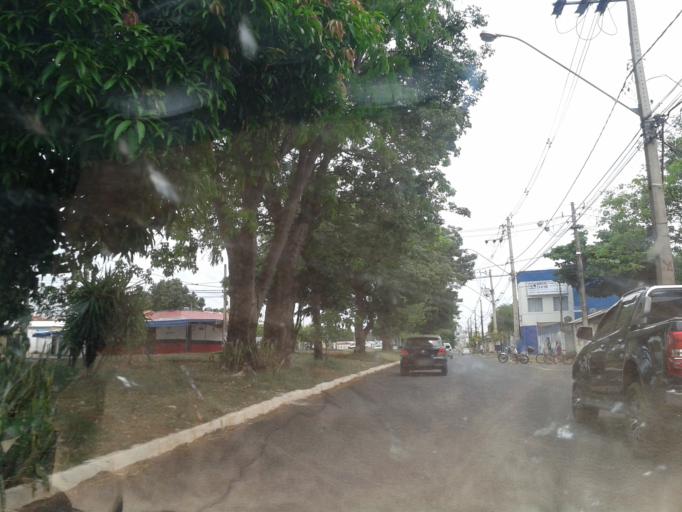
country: BR
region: Minas Gerais
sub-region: Uberlandia
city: Uberlandia
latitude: -18.9208
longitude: -48.3086
